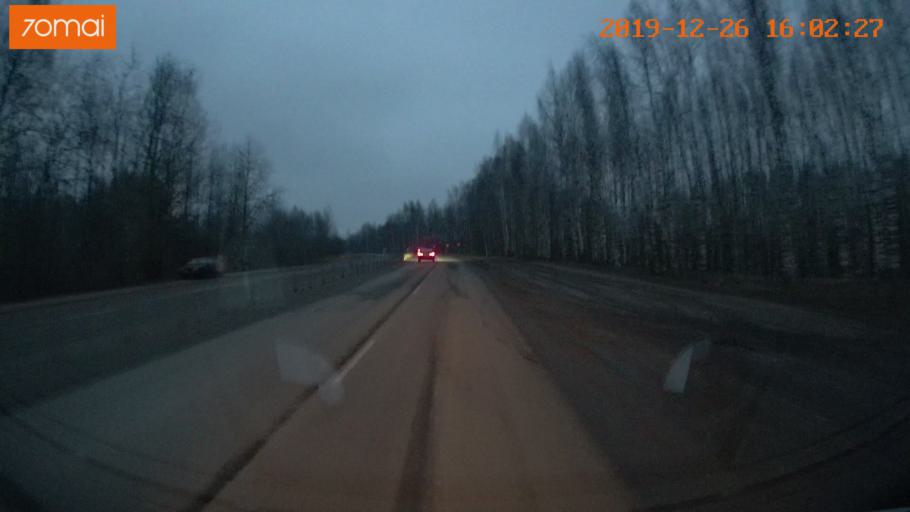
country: RU
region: Jaroslavl
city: Rybinsk
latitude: 58.0115
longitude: 38.8350
